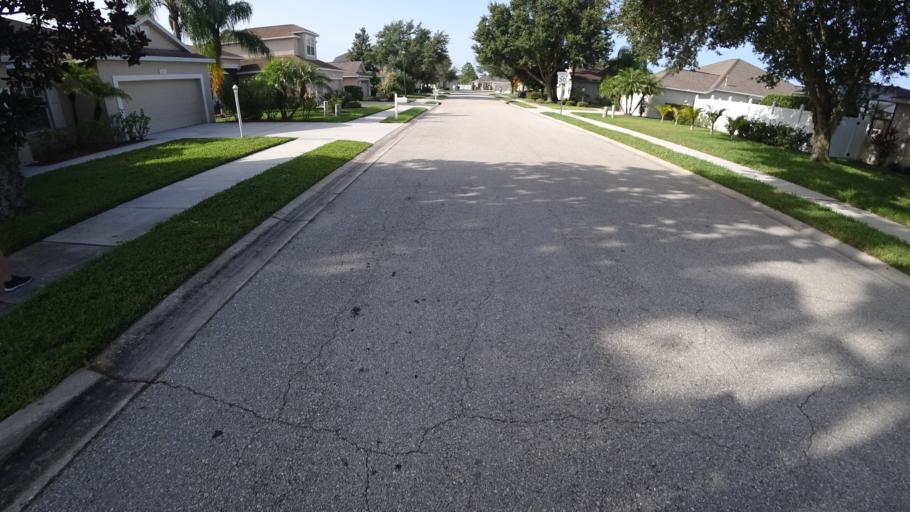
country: US
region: Florida
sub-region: Sarasota County
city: Desoto Lakes
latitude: 27.4267
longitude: -82.4716
